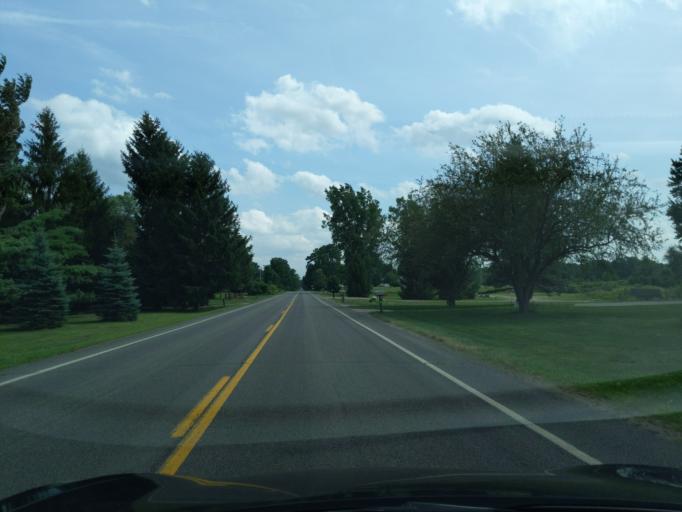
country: US
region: Michigan
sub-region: Eaton County
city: Dimondale
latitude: 42.6120
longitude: -84.6027
